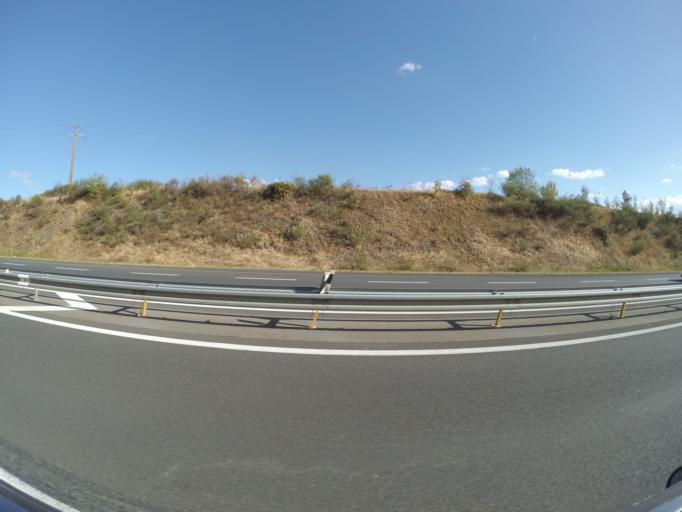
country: FR
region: Pays de la Loire
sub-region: Departement de Maine-et-Loire
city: Vihiers
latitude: 47.1384
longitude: -0.5241
